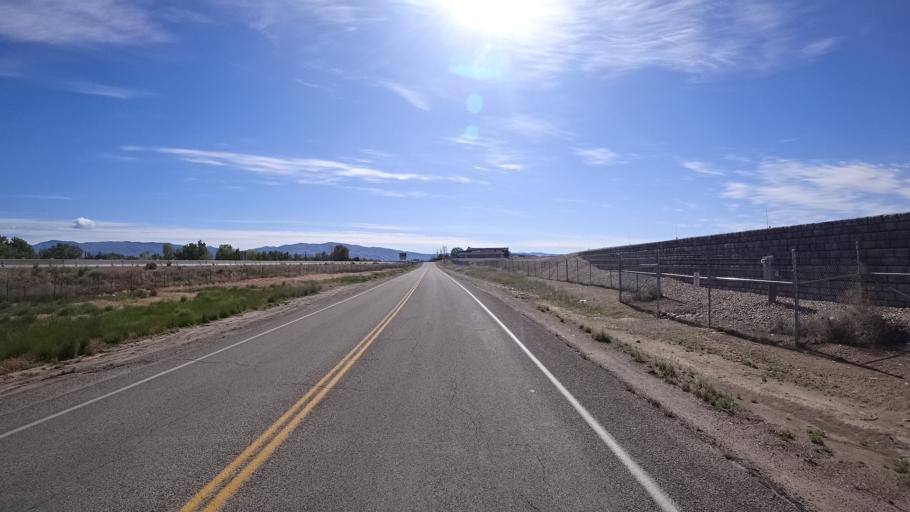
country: US
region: Idaho
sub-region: Ada County
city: Garden City
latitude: 43.5715
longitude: -116.2365
